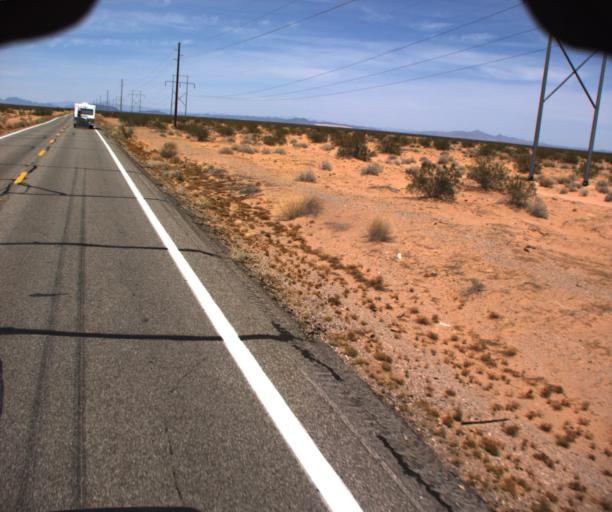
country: US
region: Arizona
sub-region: La Paz County
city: Quartzsite
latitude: 33.8950
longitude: -114.2169
